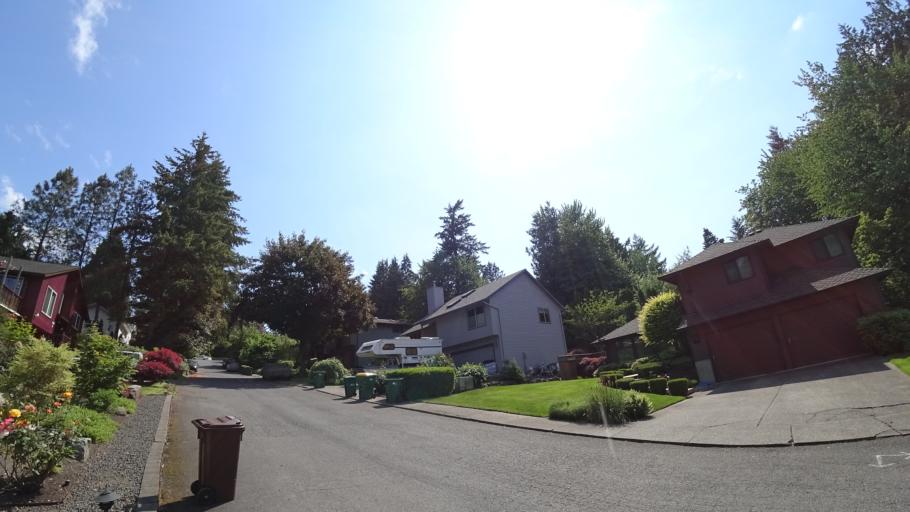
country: US
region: Oregon
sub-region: Washington County
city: Metzger
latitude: 45.4474
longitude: -122.7503
